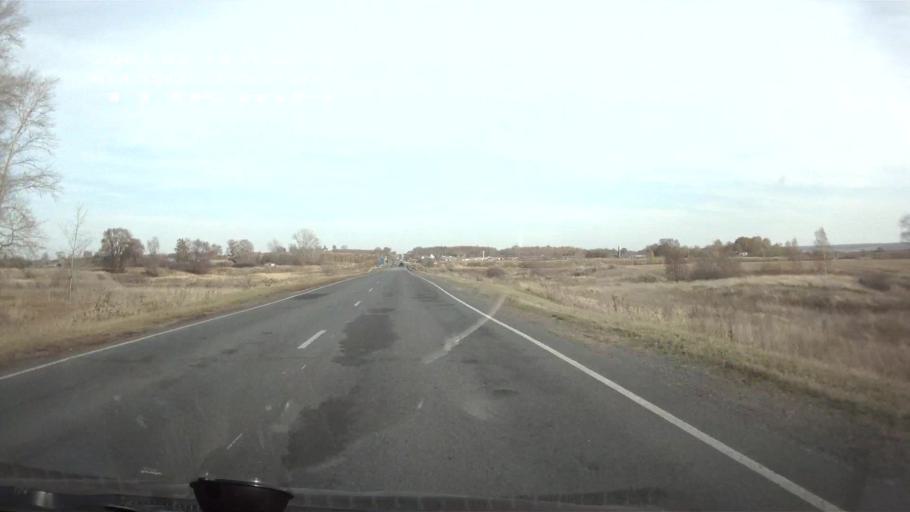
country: RU
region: Mordoviya
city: Atyashevo
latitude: 54.5543
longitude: 45.9635
